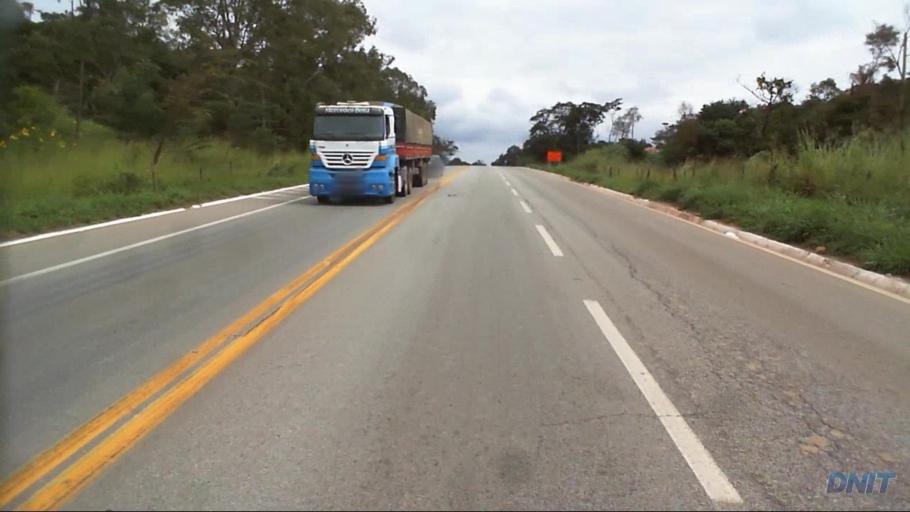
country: BR
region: Minas Gerais
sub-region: Caete
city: Caete
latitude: -19.7699
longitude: -43.6480
